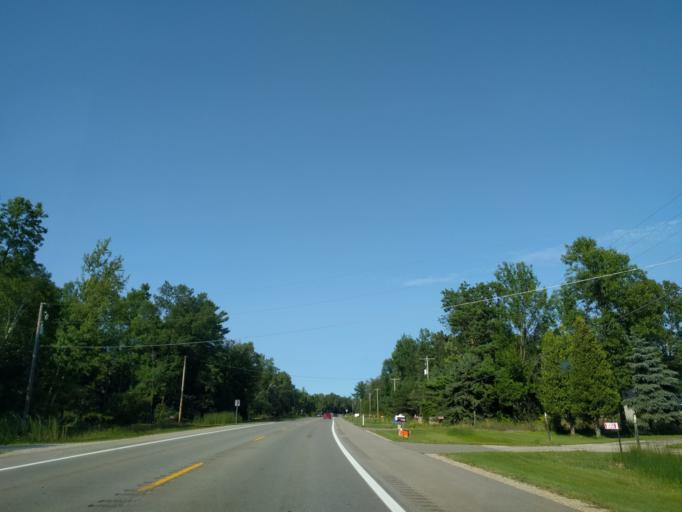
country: US
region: Michigan
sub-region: Menominee County
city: Menominee
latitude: 45.1636
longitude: -87.5892
